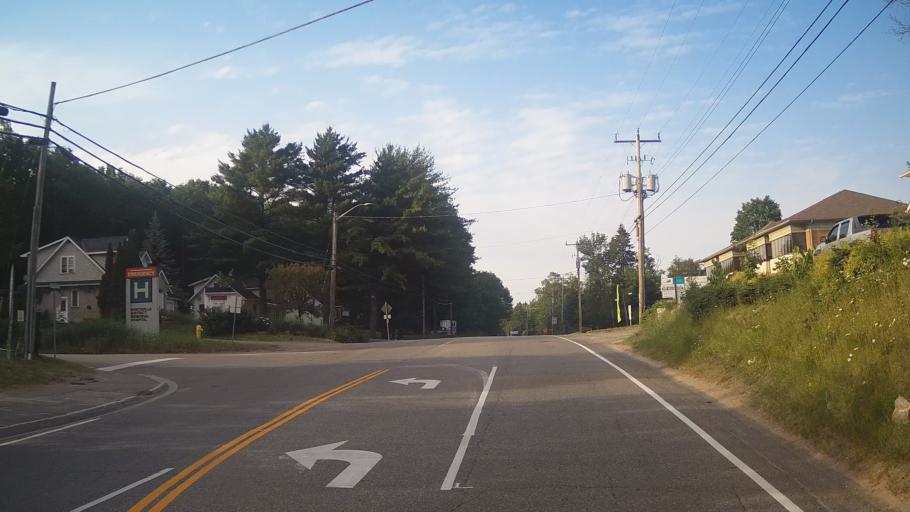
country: CA
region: Ontario
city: Huntsville
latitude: 45.3383
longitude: -79.2027
